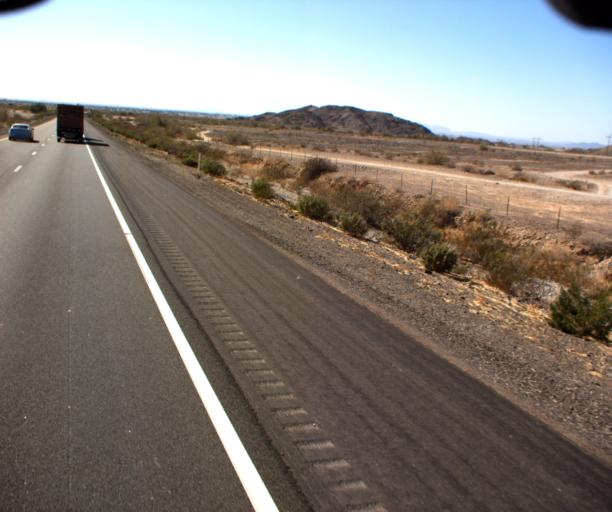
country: US
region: Arizona
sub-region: Yuma County
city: Fortuna Foothills
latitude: 32.6608
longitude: -114.3604
